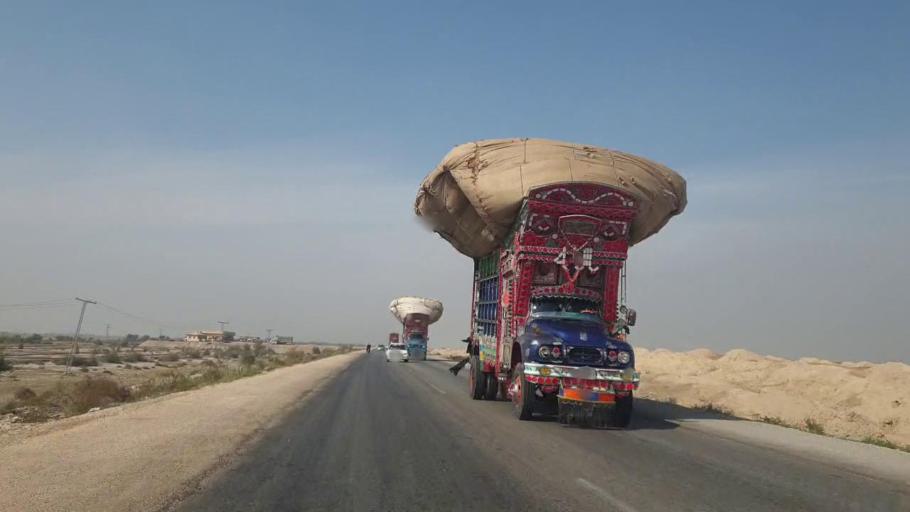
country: PK
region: Sindh
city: Sann
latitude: 25.9300
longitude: 68.2104
